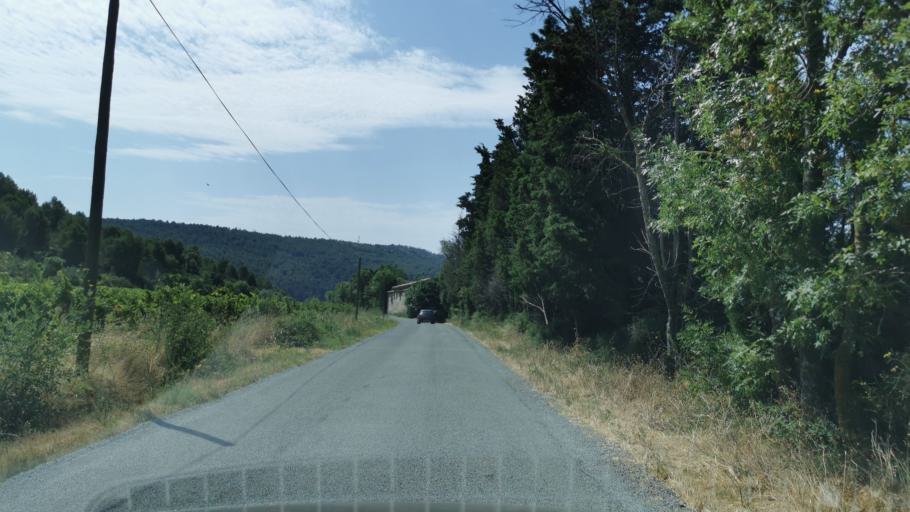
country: FR
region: Languedoc-Roussillon
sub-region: Departement de l'Aude
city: Bize-Minervois
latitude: 43.3323
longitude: 2.8770
